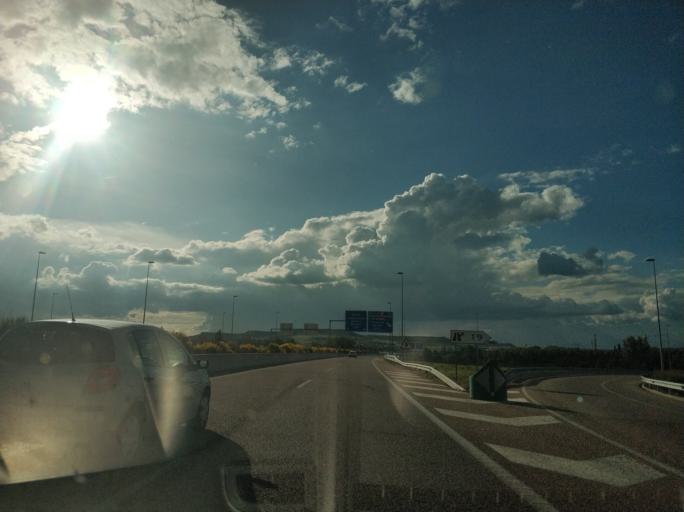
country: ES
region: Castille and Leon
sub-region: Provincia de Valladolid
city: Arroyo
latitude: 41.6115
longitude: -4.7710
